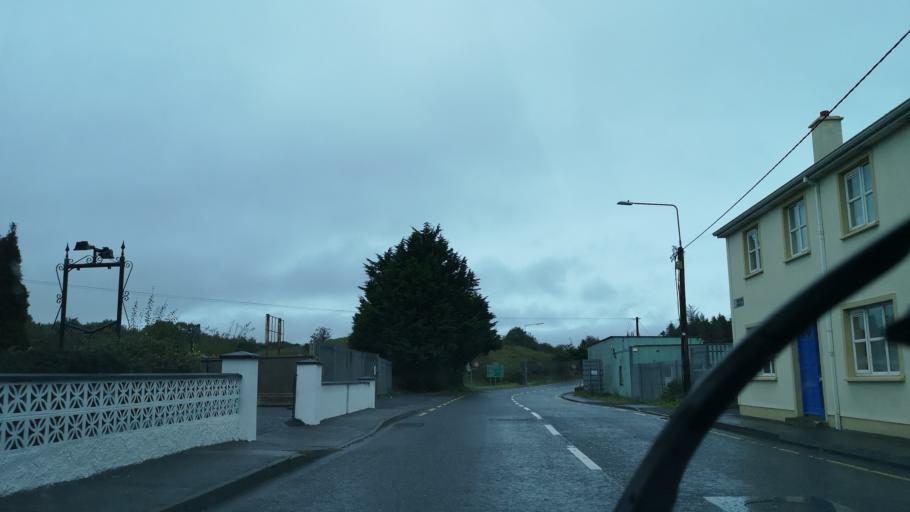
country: IE
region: Connaught
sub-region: Maigh Eo
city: Ballyhaunis
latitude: 53.7652
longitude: -8.7650
